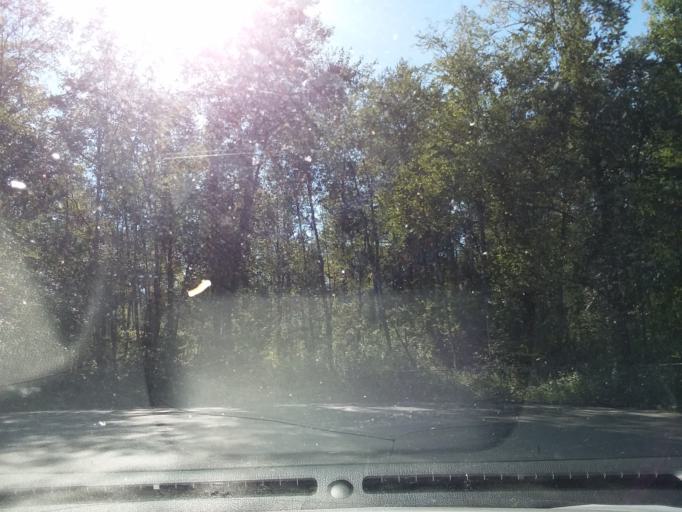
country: US
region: Washington
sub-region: Snohomish County
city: Smokey Point
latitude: 48.1605
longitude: -122.1964
